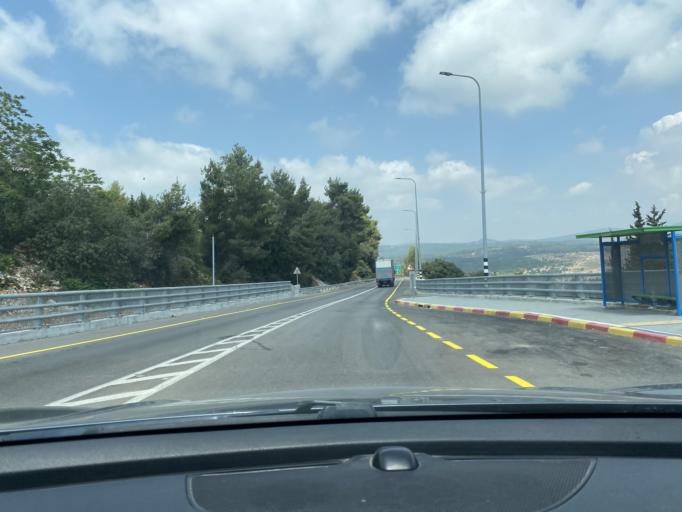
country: IL
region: Northern District
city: Kefar Weradim
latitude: 33.0017
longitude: 35.2825
